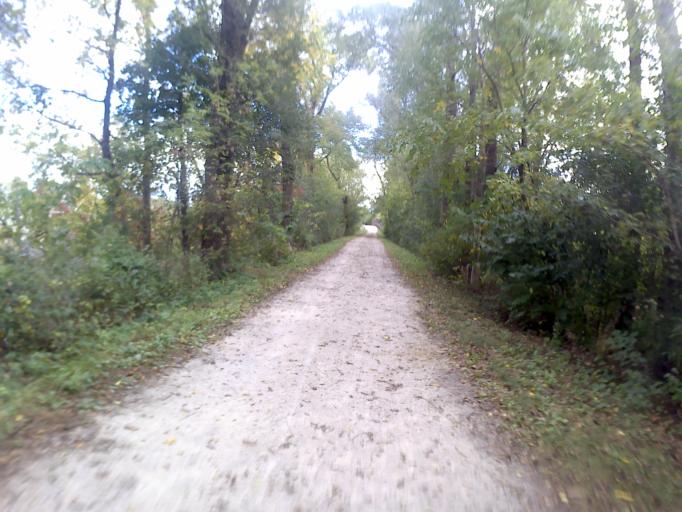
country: US
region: Illinois
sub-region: DuPage County
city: Wayne
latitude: 41.9484
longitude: -88.2386
